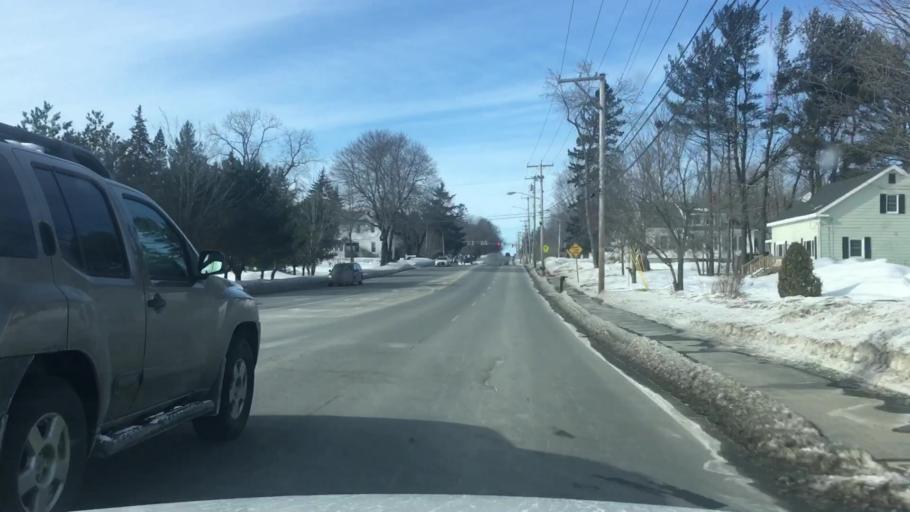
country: US
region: Maine
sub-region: Penobscot County
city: Bangor
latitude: 44.8257
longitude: -68.7814
